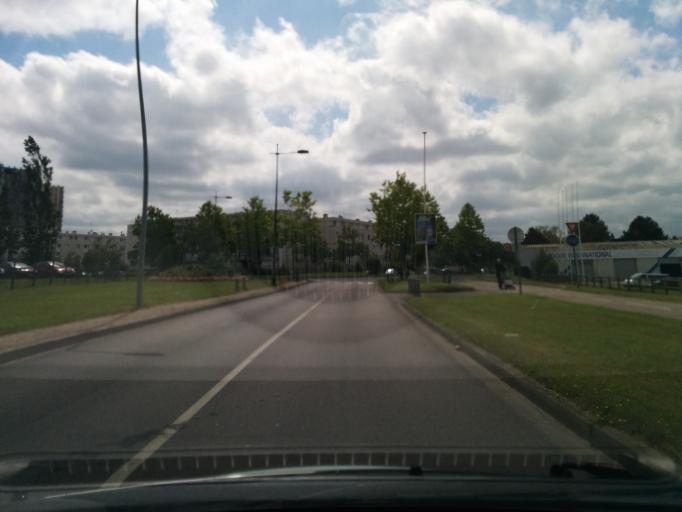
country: FR
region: Ile-de-France
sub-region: Departement des Yvelines
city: Follainville-Dennemont
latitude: 49.0057
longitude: 1.6932
